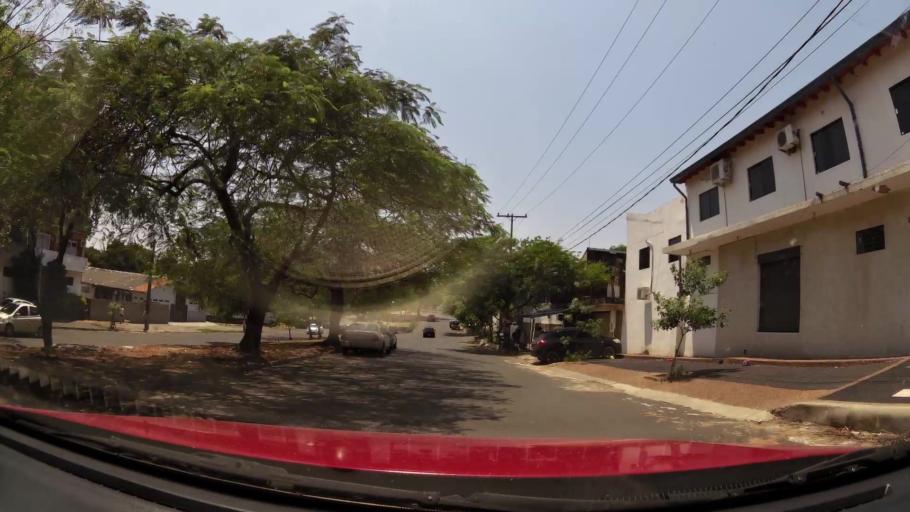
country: PY
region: Asuncion
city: Asuncion
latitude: -25.3044
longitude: -57.6382
